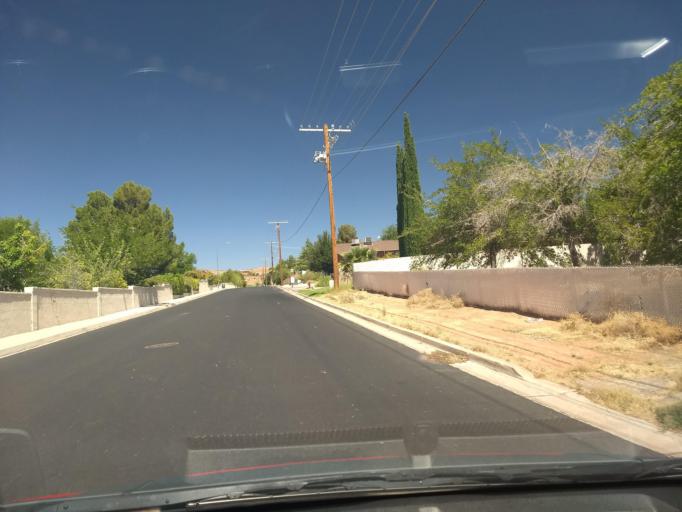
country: US
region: Utah
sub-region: Washington County
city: Washington
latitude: 37.1337
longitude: -113.5222
